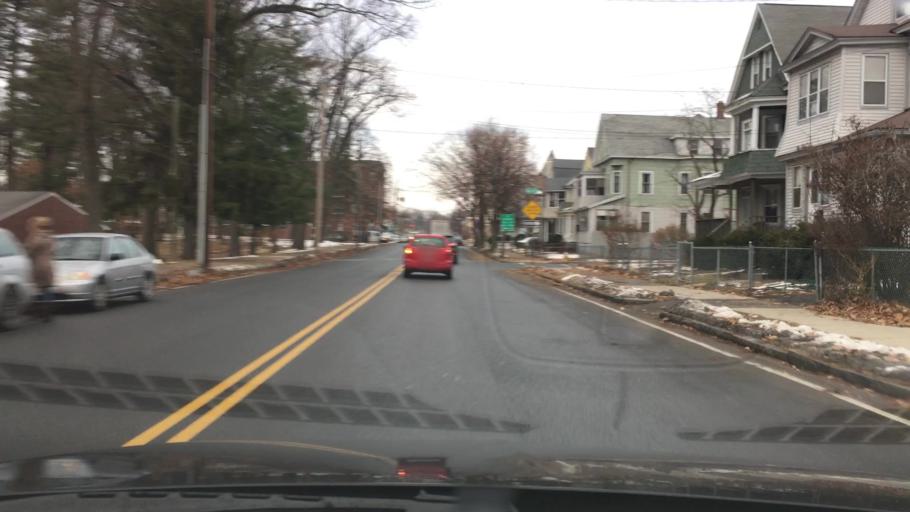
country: US
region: Massachusetts
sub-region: Hampden County
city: Springfield
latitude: 42.0840
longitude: -72.5555
